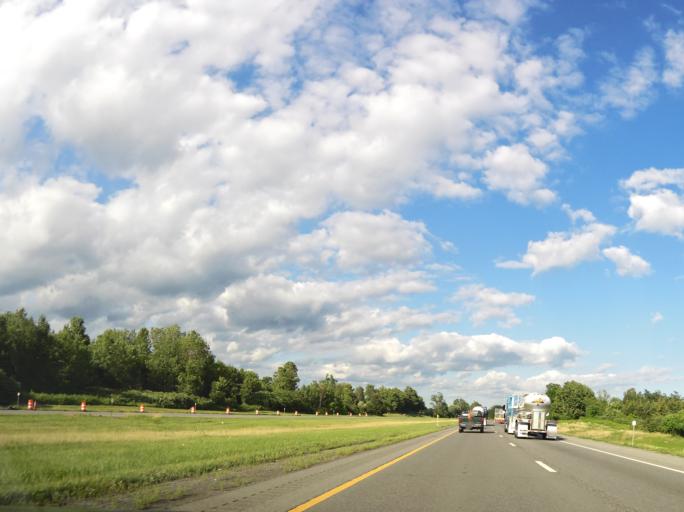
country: US
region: New York
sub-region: Erie County
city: Akron
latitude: 42.9790
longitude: -78.5016
